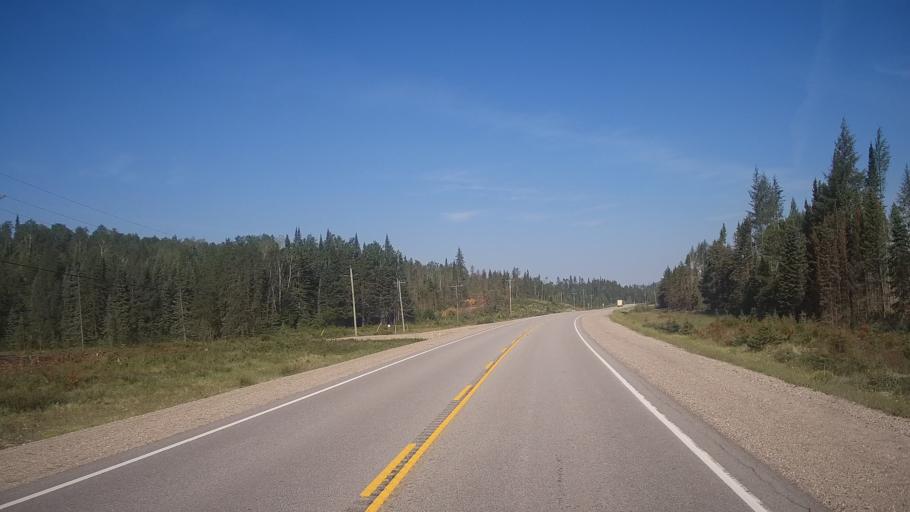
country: CA
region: Ontario
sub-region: Rainy River District
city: Atikokan
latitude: 49.4595
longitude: -91.8702
